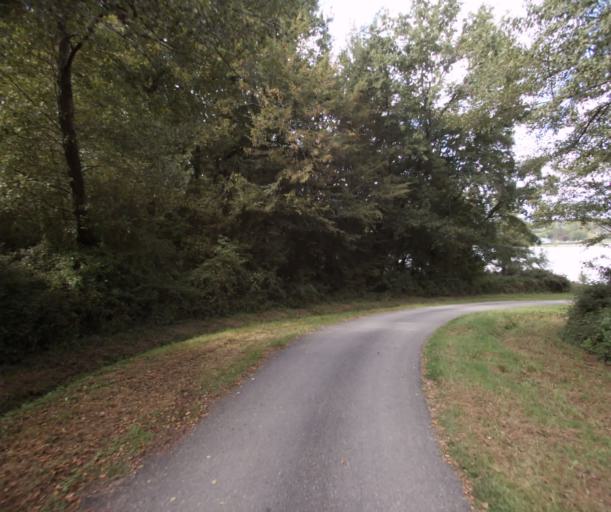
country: FR
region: Midi-Pyrenees
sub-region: Departement du Gers
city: Cazaubon
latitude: 43.9340
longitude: -0.0434
